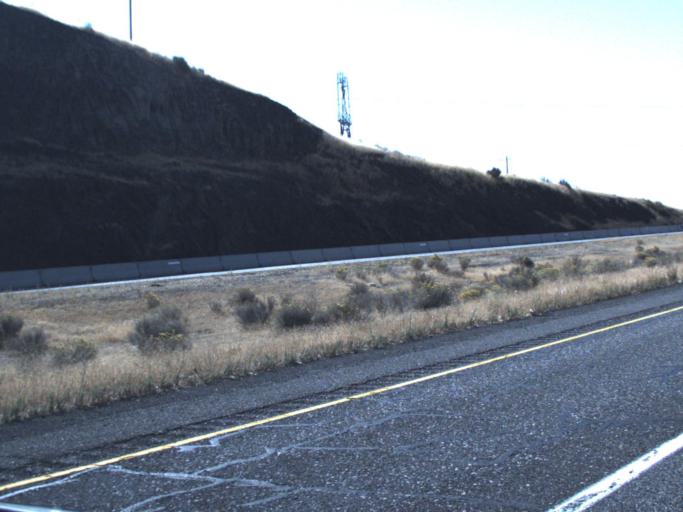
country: US
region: Washington
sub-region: Franklin County
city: Basin City
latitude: 46.5457
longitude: -119.0073
